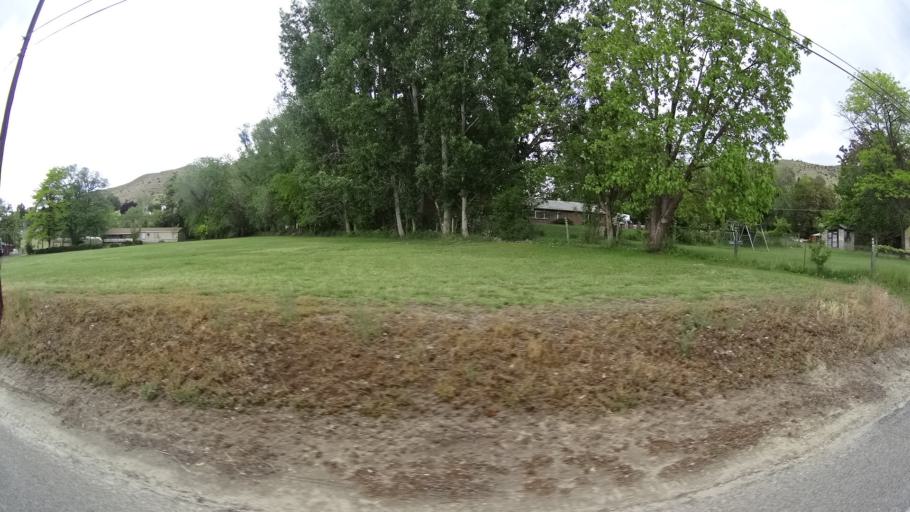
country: US
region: Idaho
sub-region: Ada County
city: Garden City
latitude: 43.6742
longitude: -116.2603
